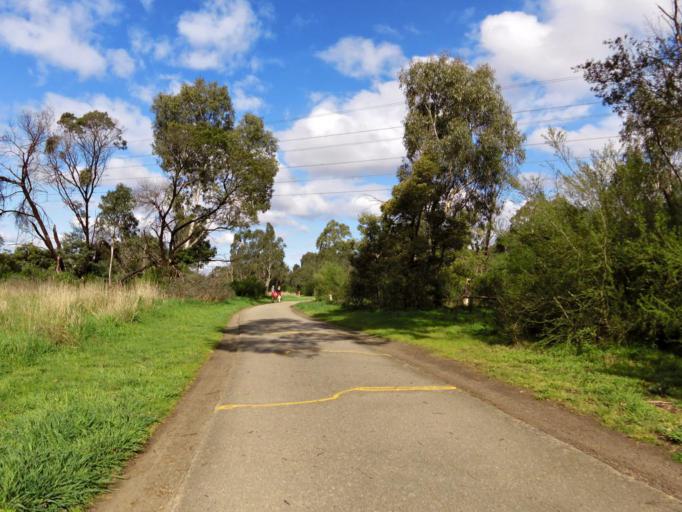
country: AU
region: Victoria
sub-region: Banyule
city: Viewbank
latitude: -37.7516
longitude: 145.1017
